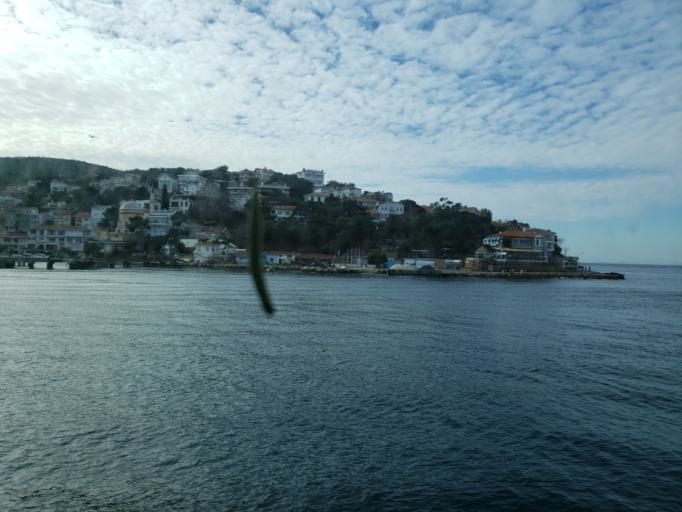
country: TR
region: Istanbul
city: Adalan
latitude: 40.8838
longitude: 29.0713
